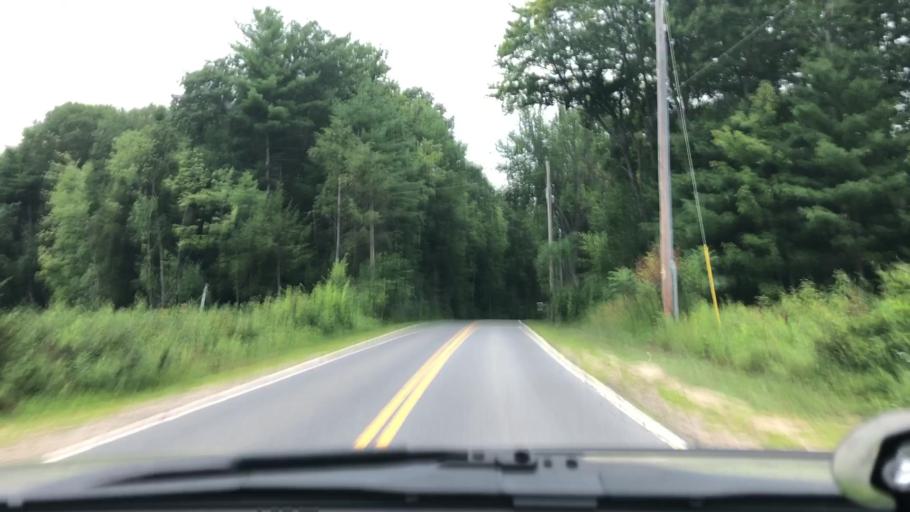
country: US
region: New York
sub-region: Saratoga County
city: Corinth
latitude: 43.2141
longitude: -73.8014
